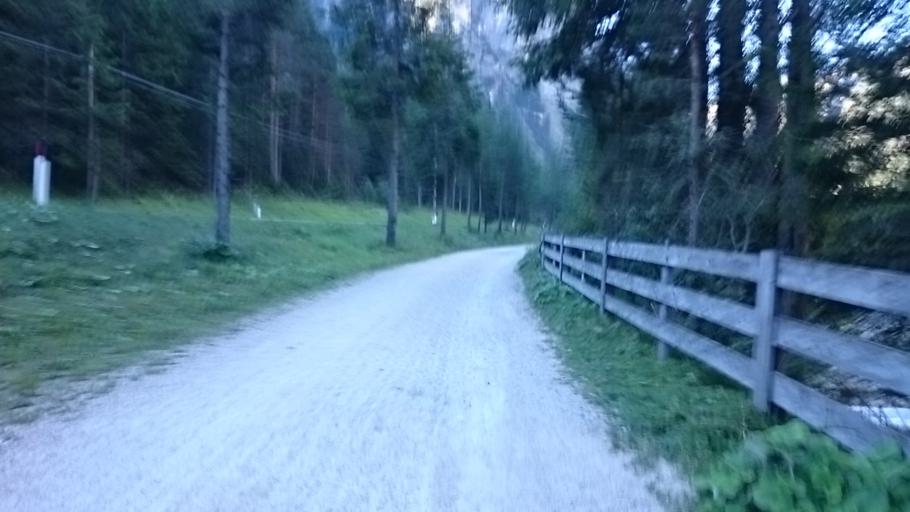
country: IT
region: Trentino-Alto Adige
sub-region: Bolzano
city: Dobbiaco
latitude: 46.6858
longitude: 12.2243
